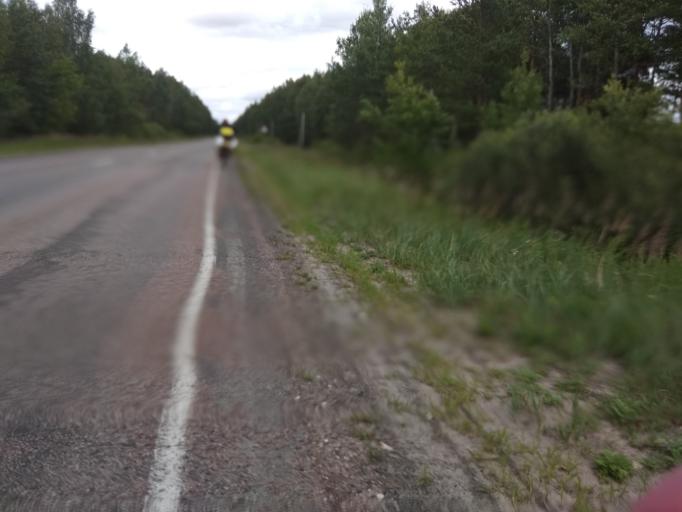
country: RU
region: Moskovskaya
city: Misheronskiy
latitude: 55.6093
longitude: 39.7146
